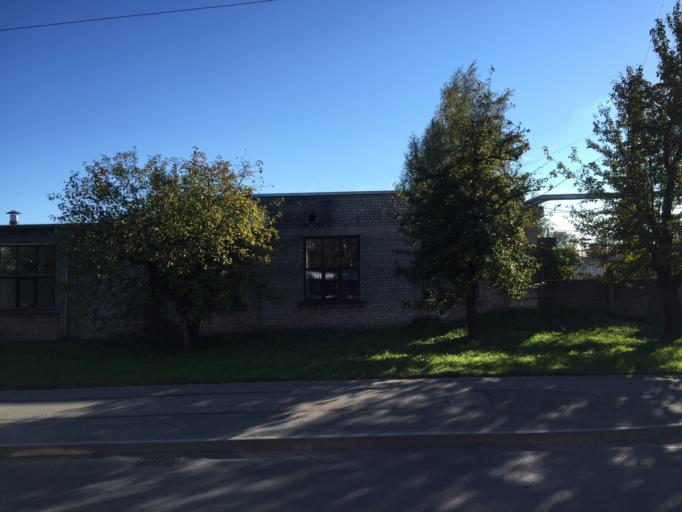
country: LV
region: Riga
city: Riga
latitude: 56.9884
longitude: 24.1257
